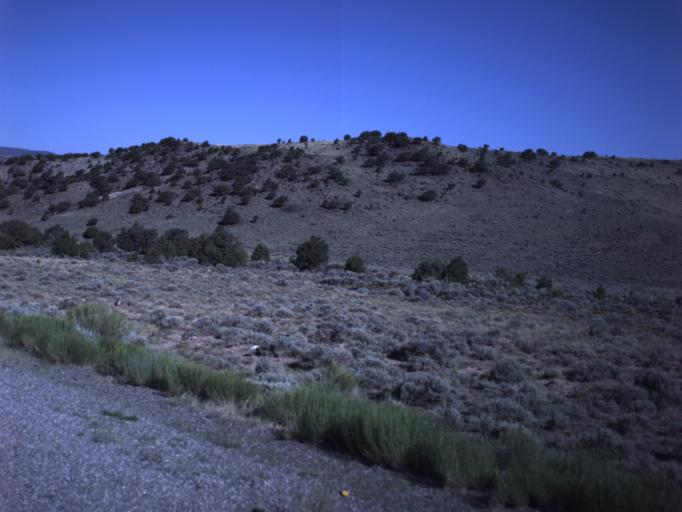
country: US
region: Utah
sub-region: Wayne County
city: Loa
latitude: 38.4793
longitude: -111.5632
